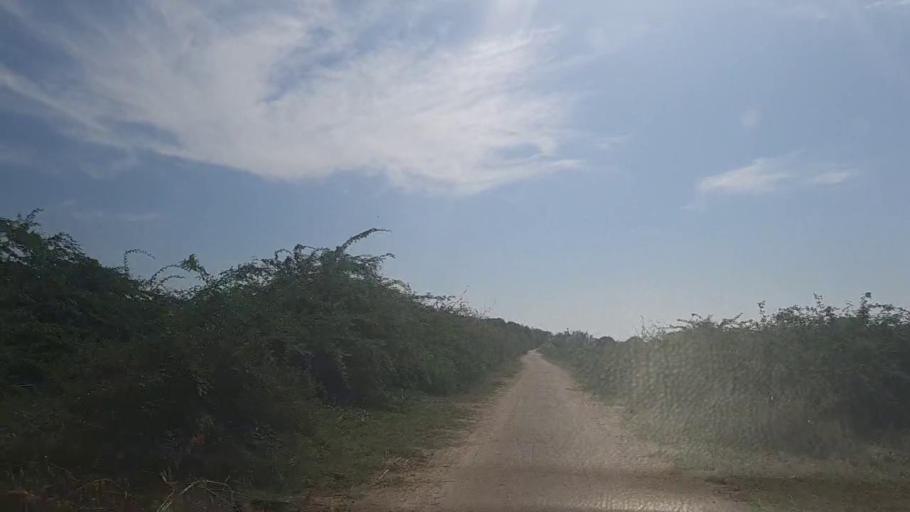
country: PK
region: Sindh
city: Mirpur Batoro
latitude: 24.6669
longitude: 68.1844
